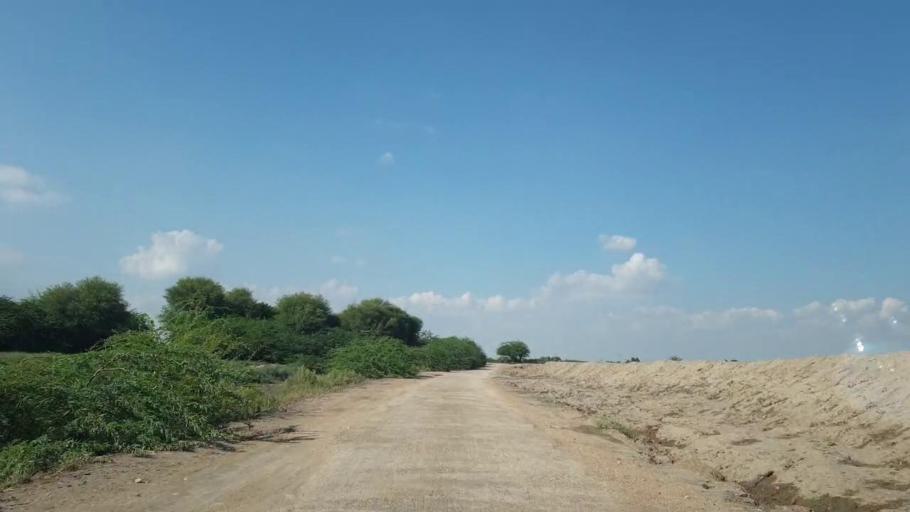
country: PK
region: Sindh
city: Pithoro
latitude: 25.6353
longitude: 69.4382
